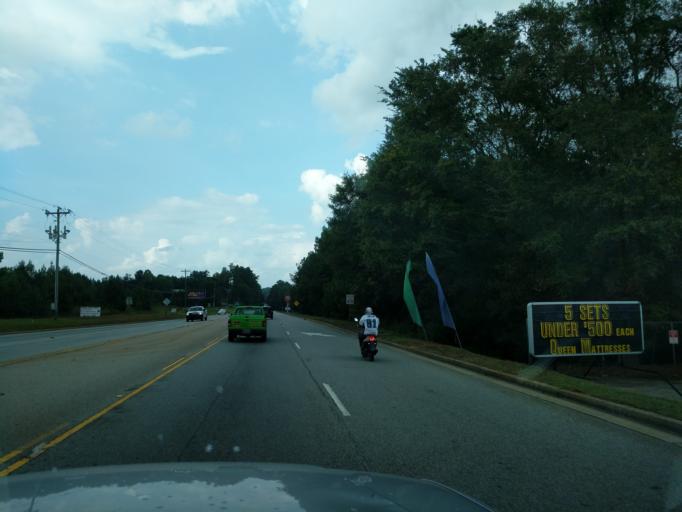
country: US
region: South Carolina
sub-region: Anderson County
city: Northlake
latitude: 34.5623
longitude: -82.6882
